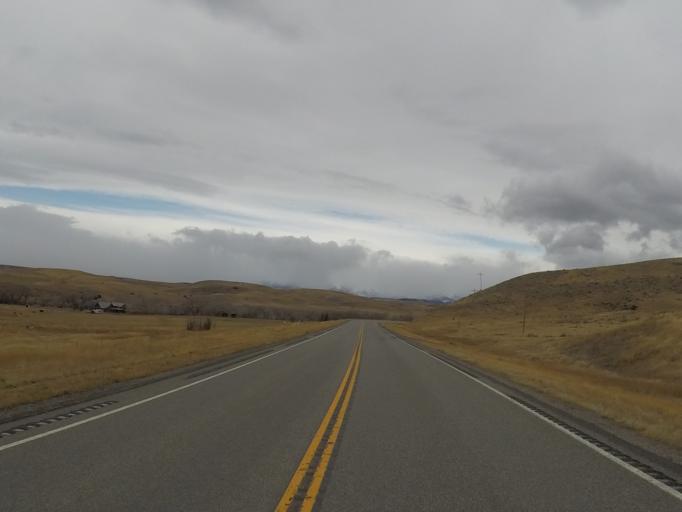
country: US
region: Montana
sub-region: Sweet Grass County
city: Big Timber
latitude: 45.8998
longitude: -109.9687
